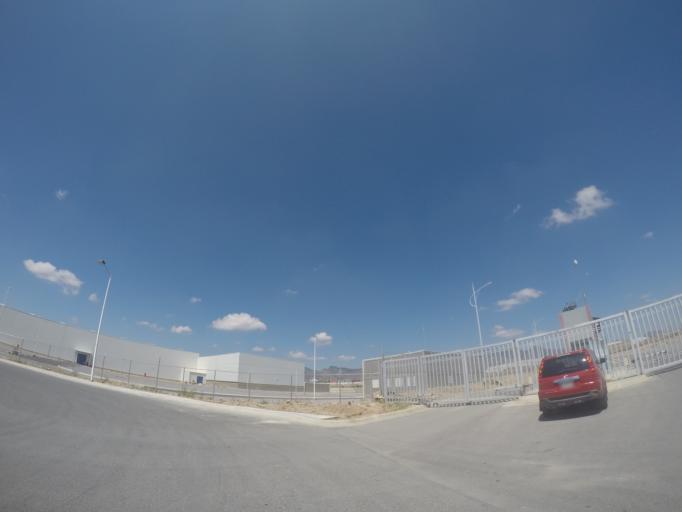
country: MX
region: San Luis Potosi
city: La Pila
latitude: 21.9762
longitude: -100.8797
